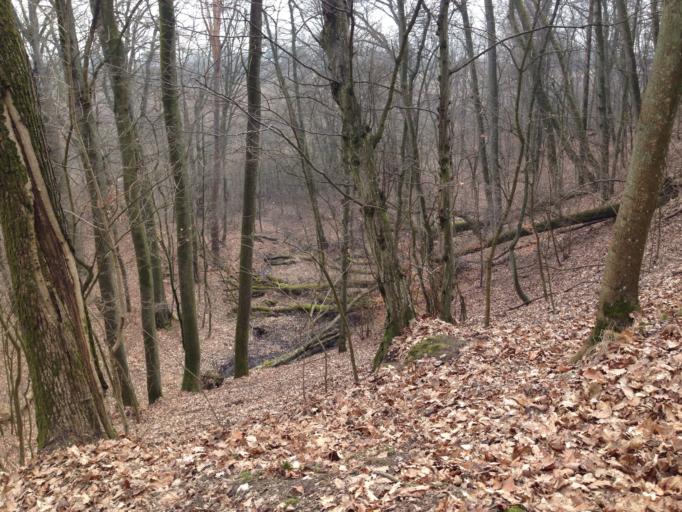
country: PL
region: Pomeranian Voivodeship
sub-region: Powiat kwidzynski
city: Sadlinki
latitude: 53.7181
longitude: 18.8115
